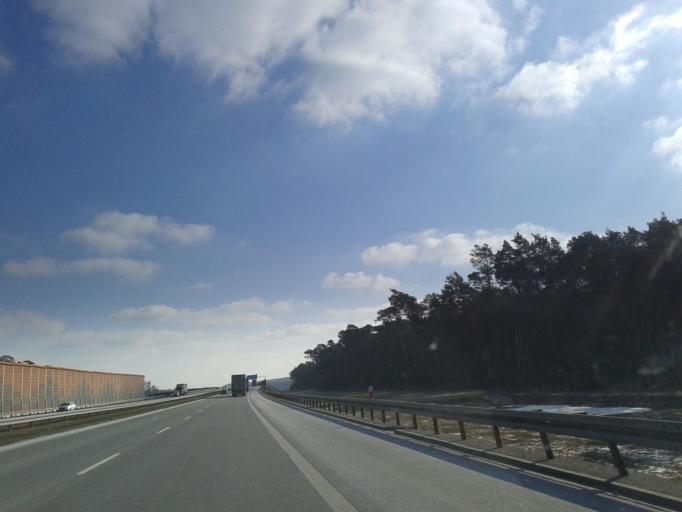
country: PL
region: Kujawsko-Pomorskie
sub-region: Powiat aleksandrowski
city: Ciechocinek
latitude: 52.8774
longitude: 18.7463
